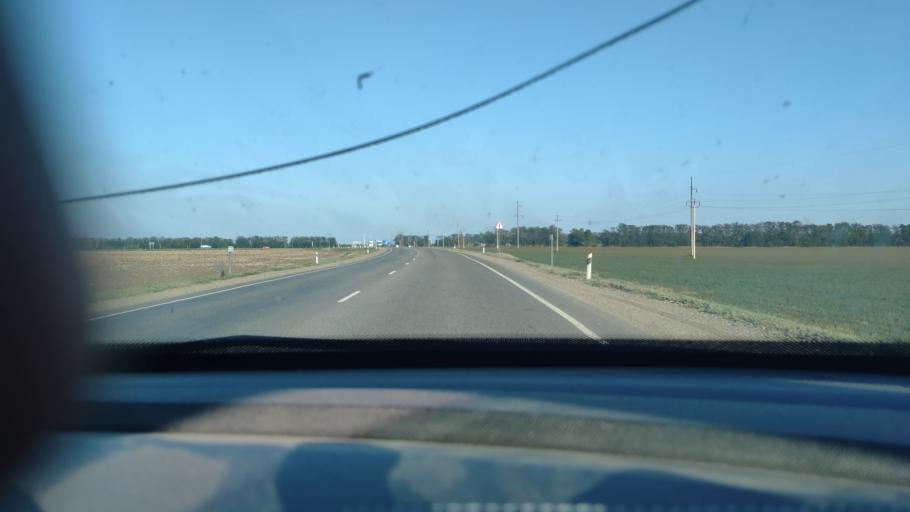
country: RU
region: Krasnodarskiy
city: Staroshcherbinovskaya
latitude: 46.6106
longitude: 38.6435
